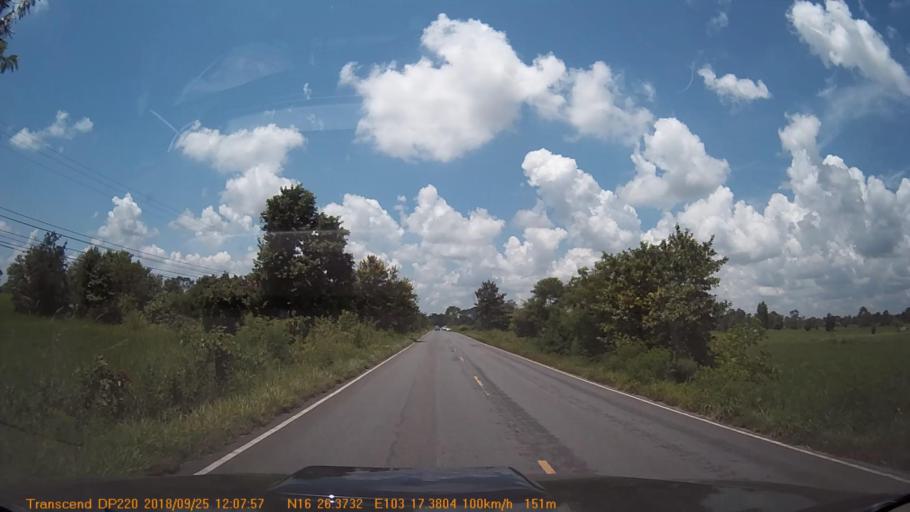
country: TH
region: Kalasin
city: Yang Talat
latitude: 16.4396
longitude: 103.2896
